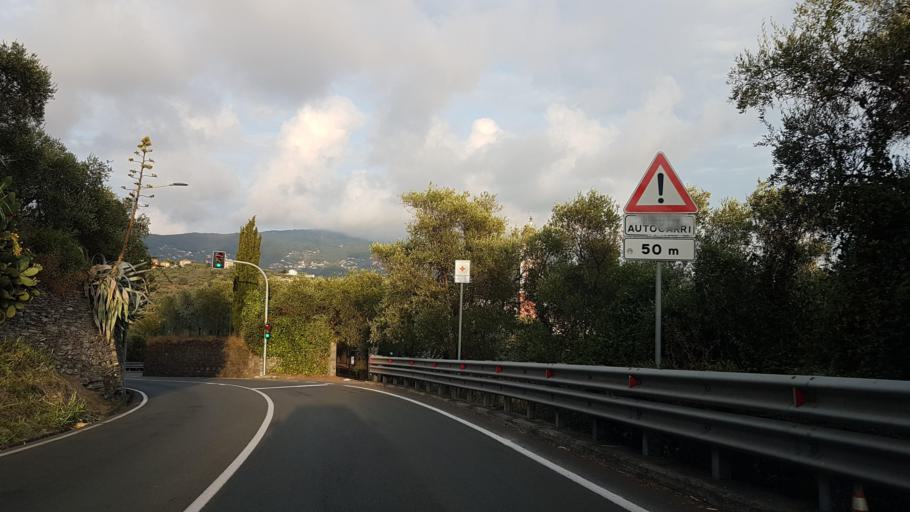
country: IT
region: Liguria
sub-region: Provincia di Genova
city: Chiavari
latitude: 44.3231
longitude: 9.3167
